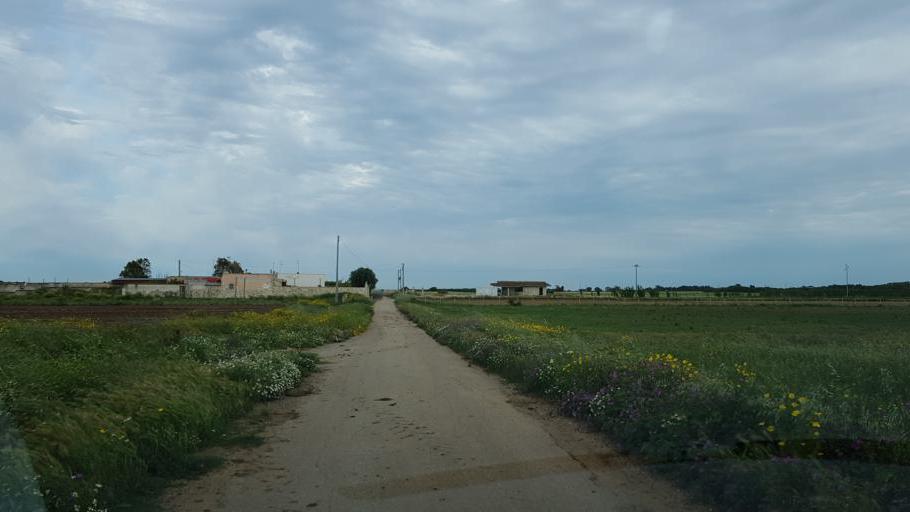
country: IT
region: Apulia
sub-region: Provincia di Brindisi
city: Brindisi
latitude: 40.6550
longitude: 17.8669
